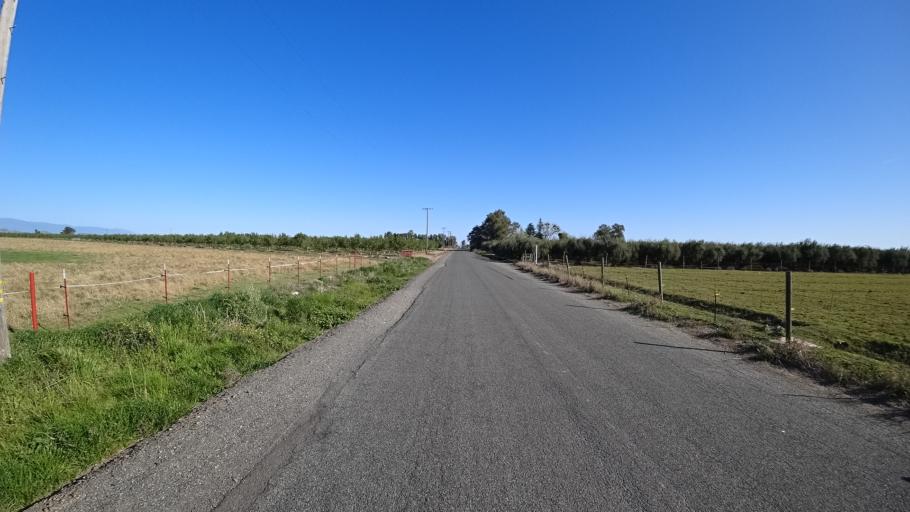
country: US
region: California
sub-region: Glenn County
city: Orland
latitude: 39.7449
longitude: -122.2389
